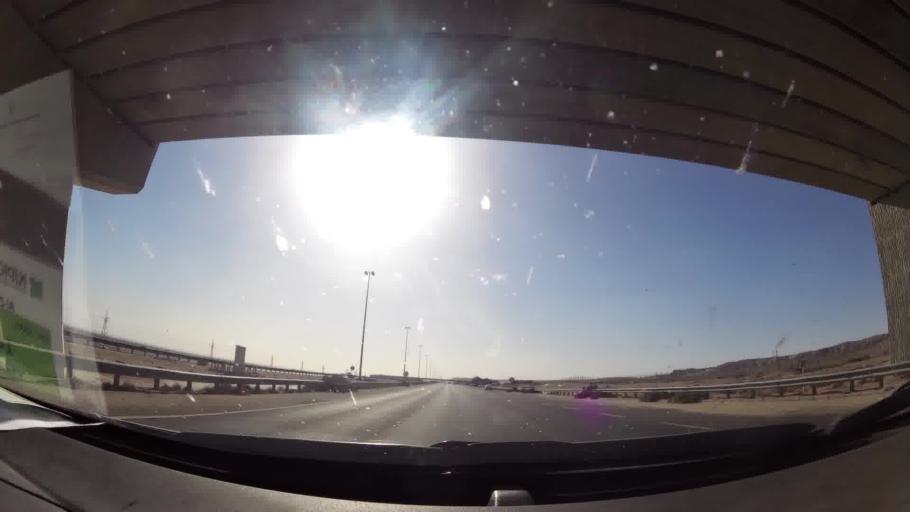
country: KW
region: Al Asimah
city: Kuwait City
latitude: 29.5280
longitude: 47.8219
